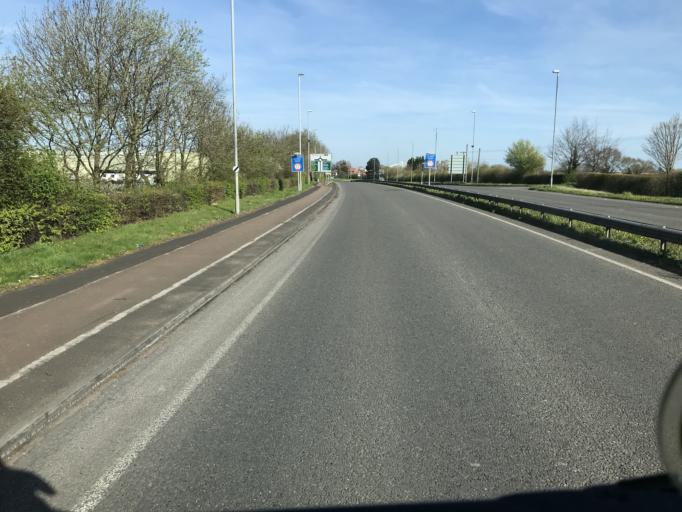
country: GB
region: England
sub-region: Cheshire West and Chester
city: Marston
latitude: 53.2472
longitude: -2.4716
